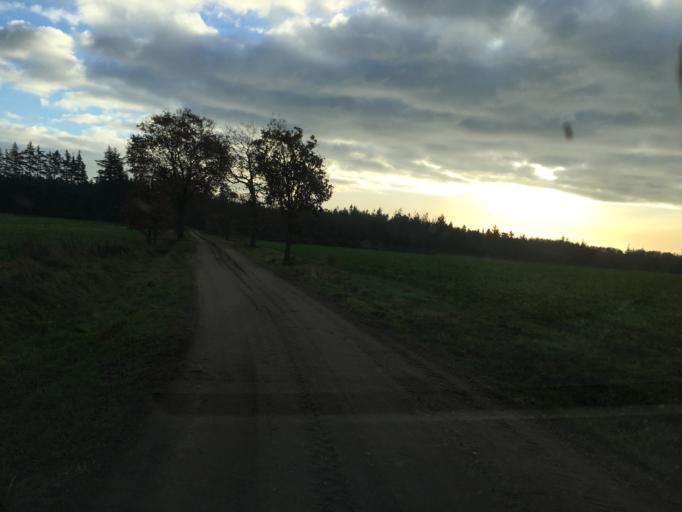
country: DK
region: South Denmark
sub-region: Tonder Kommune
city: Sherrebek
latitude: 55.1313
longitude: 8.8689
